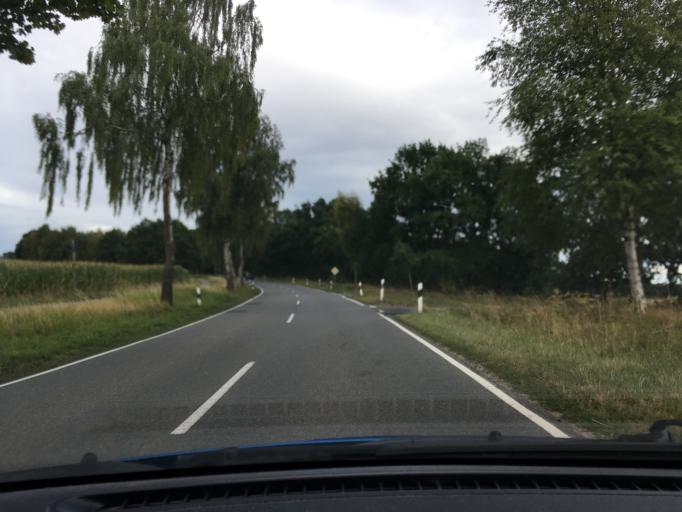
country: DE
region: Lower Saxony
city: Egestorf
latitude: 53.2031
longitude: 10.0364
